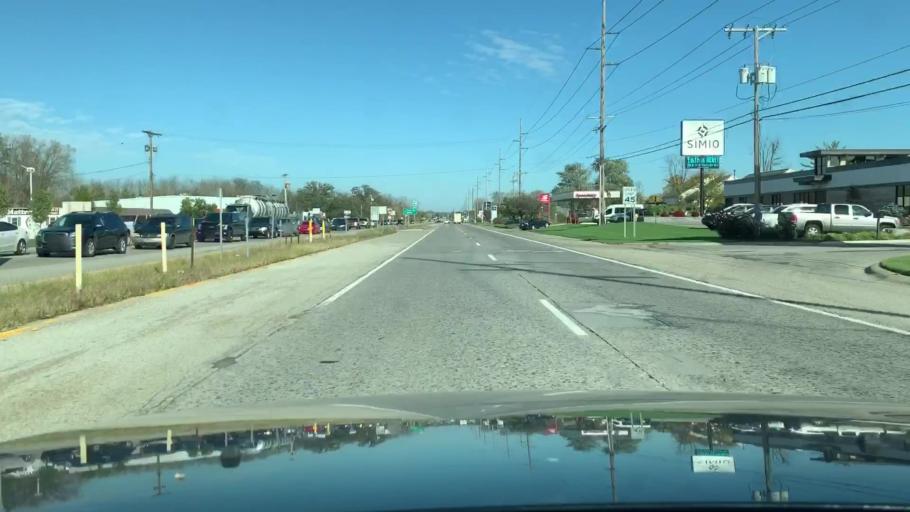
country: US
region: Michigan
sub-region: Ottawa County
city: Holland
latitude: 42.7980
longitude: -86.0770
